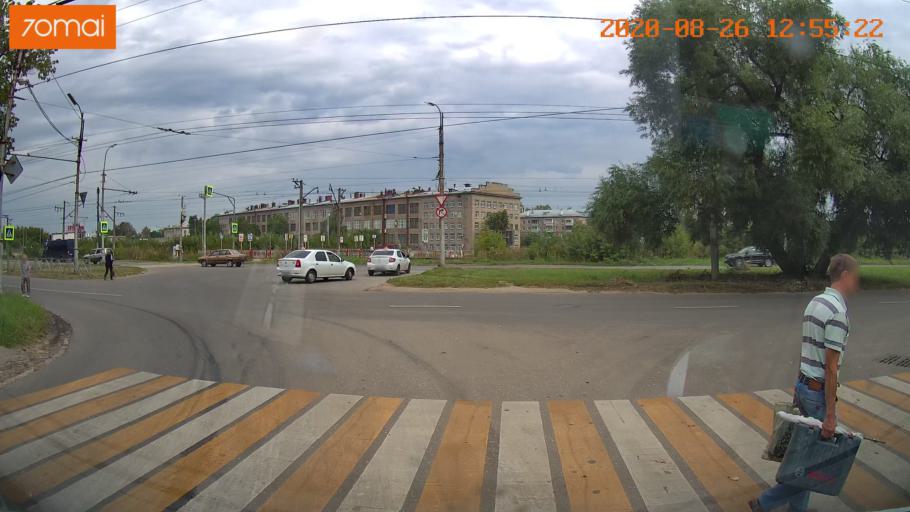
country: RU
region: Rjazan
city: Ryazan'
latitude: 54.6090
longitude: 39.7587
